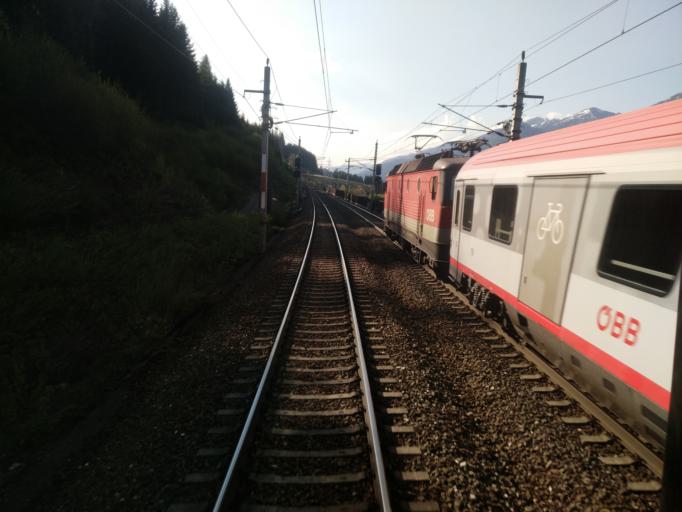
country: AT
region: Styria
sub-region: Politischer Bezirk Leoben
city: Wald am Schoberpass
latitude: 47.4447
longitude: 14.6807
